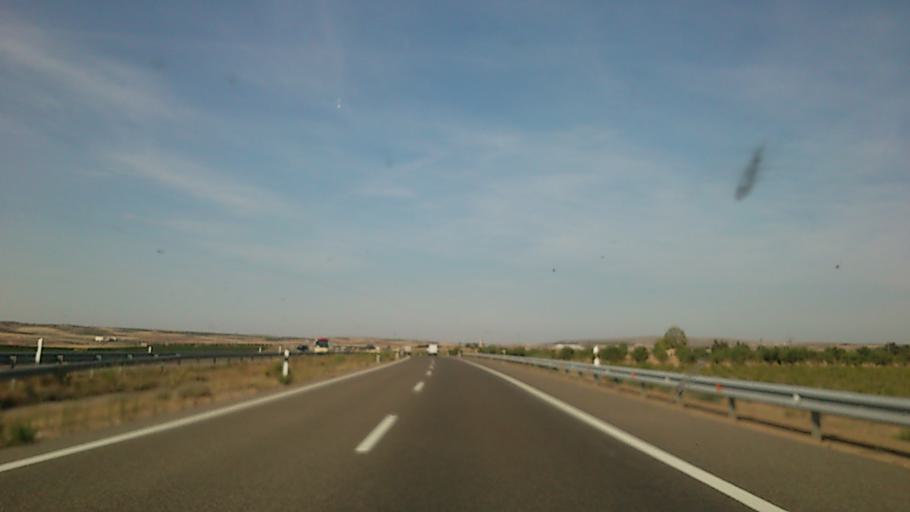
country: ES
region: Aragon
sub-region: Provincia de Zaragoza
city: Longares
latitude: 41.3846
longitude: -1.1874
